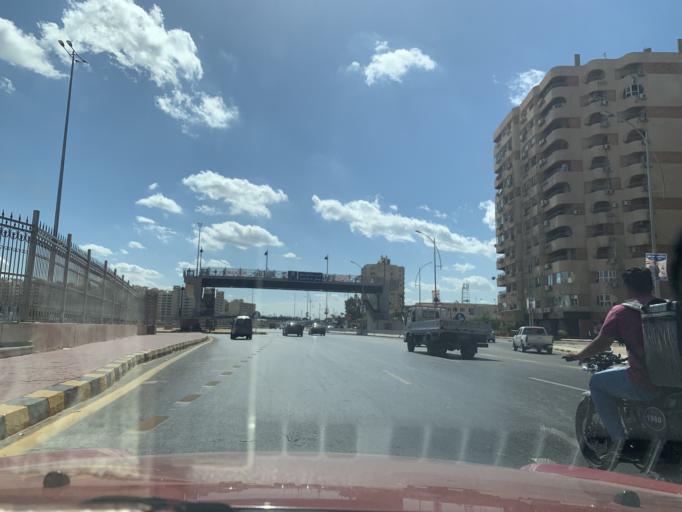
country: EG
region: Alexandria
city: Alexandria
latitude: 31.2076
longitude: 29.9549
